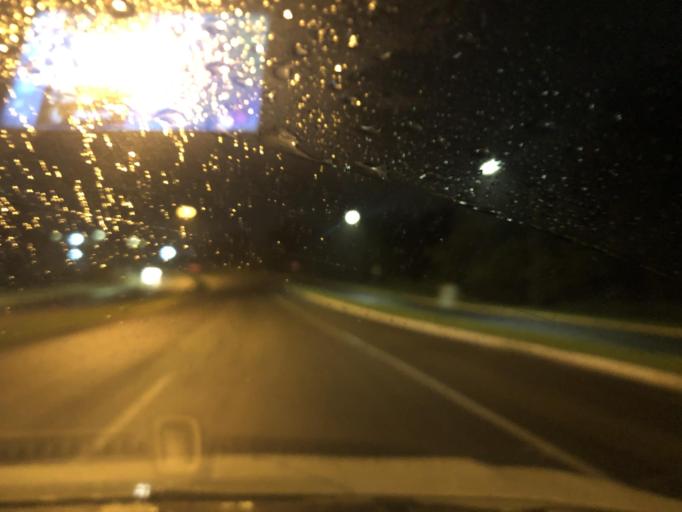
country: BR
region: Santa Catarina
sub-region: Joinville
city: Joinville
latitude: -26.3727
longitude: -48.8323
